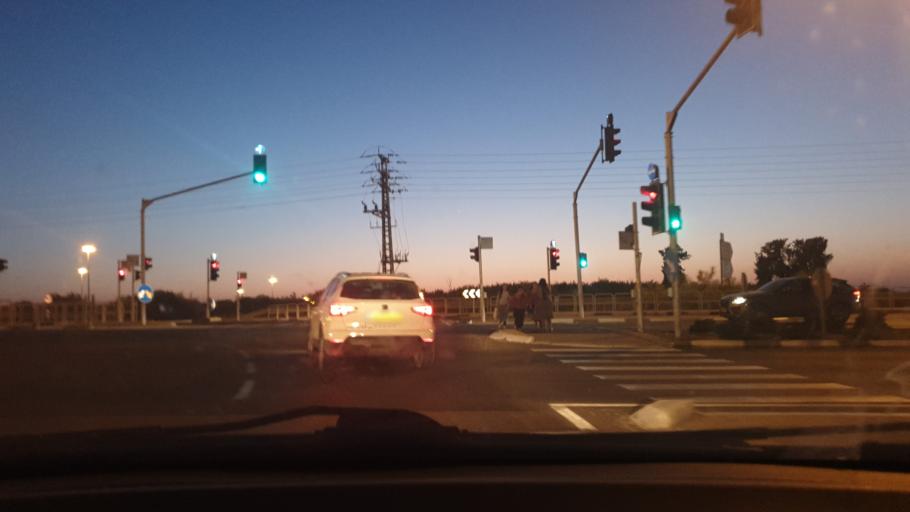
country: IL
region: Central District
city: Gedera
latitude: 31.8061
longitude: 34.7657
